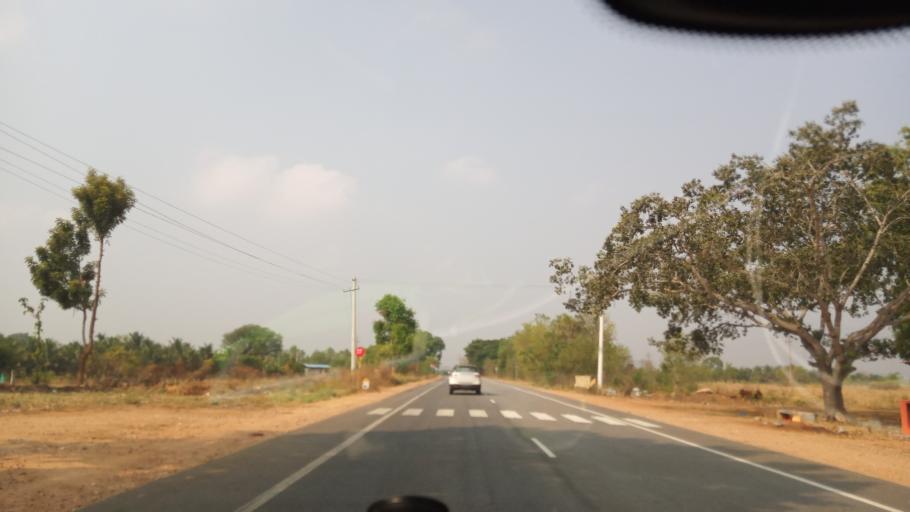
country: IN
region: Karnataka
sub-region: Mandya
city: Nagamangala
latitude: 12.7817
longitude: 76.7451
